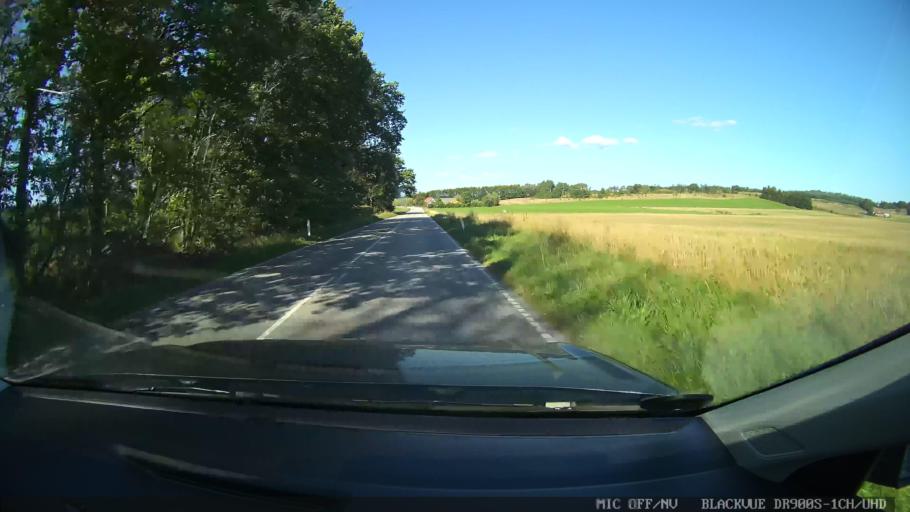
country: DK
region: North Denmark
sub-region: Mariagerfjord Kommune
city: Mariager
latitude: 56.6356
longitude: 9.9774
